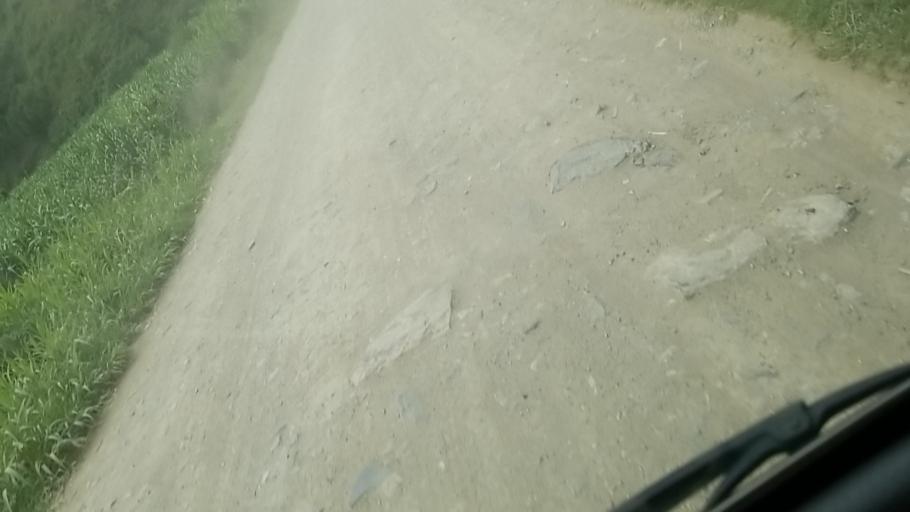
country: CD
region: Nord Kivu
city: Sake
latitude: -1.5741
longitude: 29.0434
